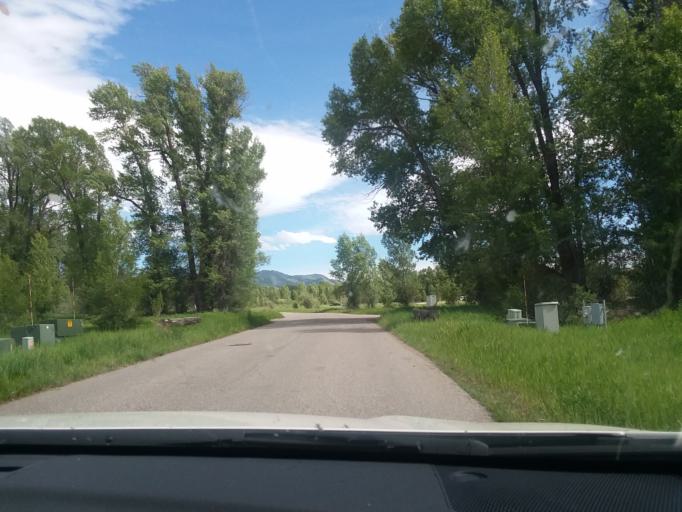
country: US
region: Wyoming
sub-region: Teton County
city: Moose Wilson Road
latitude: 43.5039
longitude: -110.8496
